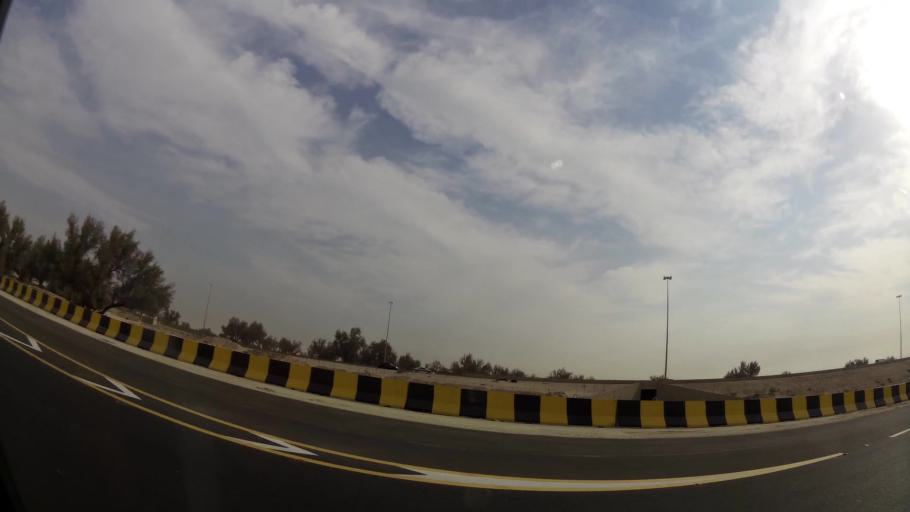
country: KW
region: Muhafazat al Jahra'
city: Al Jahra'
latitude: 29.2850
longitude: 47.7880
